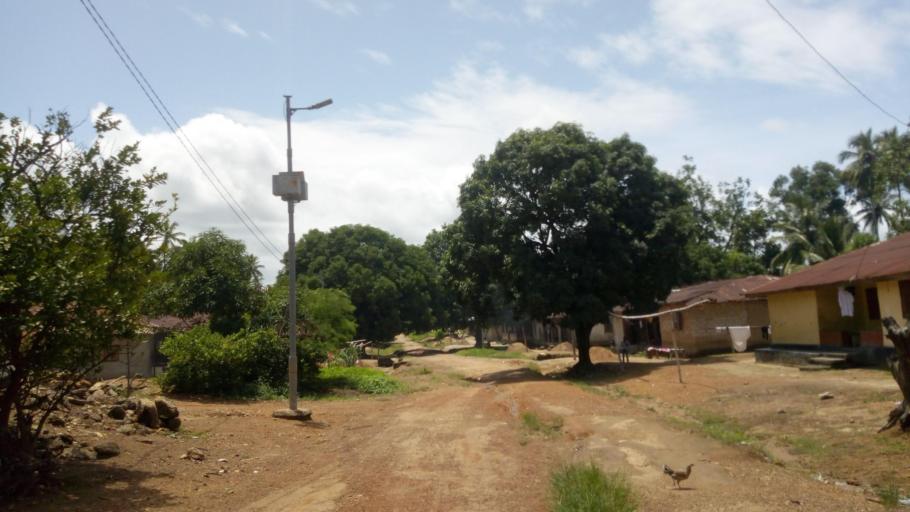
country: SL
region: Northern Province
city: Magburaka
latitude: 8.7189
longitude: -11.9576
